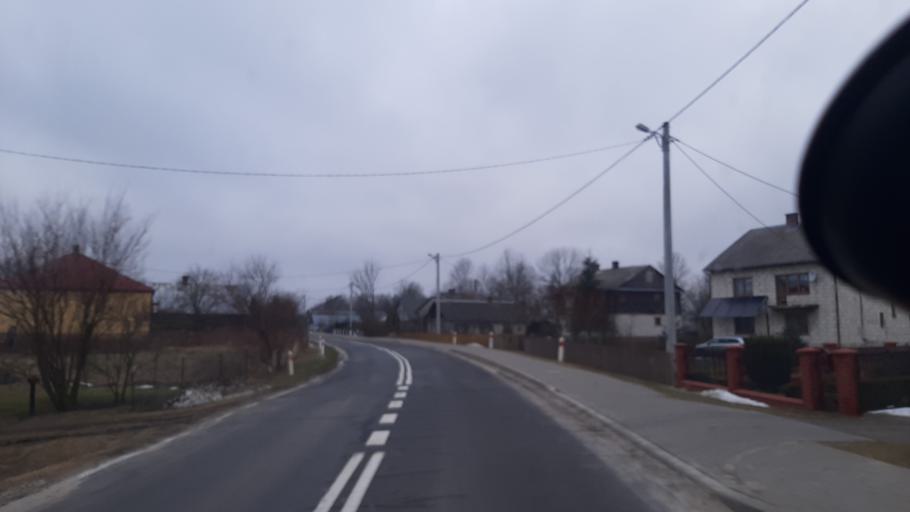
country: PL
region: Lublin Voivodeship
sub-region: Powiat wlodawski
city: Hansk
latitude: 51.5628
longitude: 23.3628
